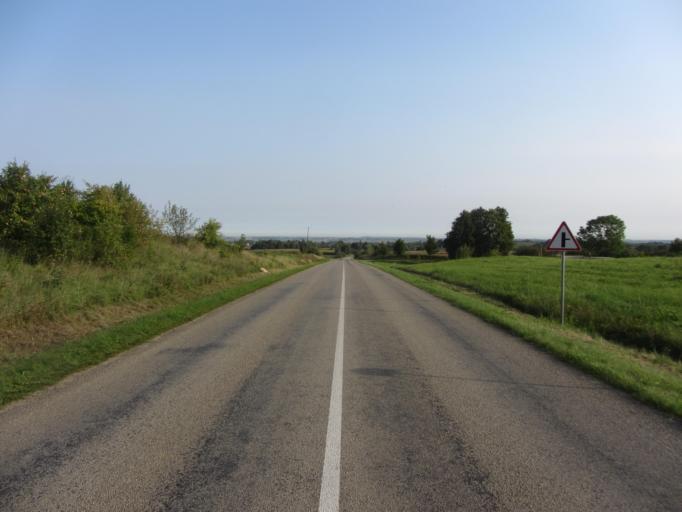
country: LT
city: Lazdijai
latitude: 54.3031
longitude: 23.4409
